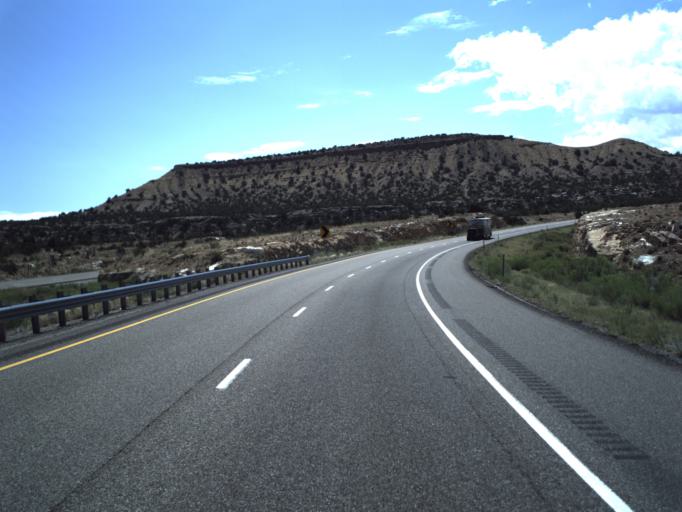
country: US
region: Utah
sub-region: Emery County
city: Castle Dale
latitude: 38.9160
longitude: -110.5027
